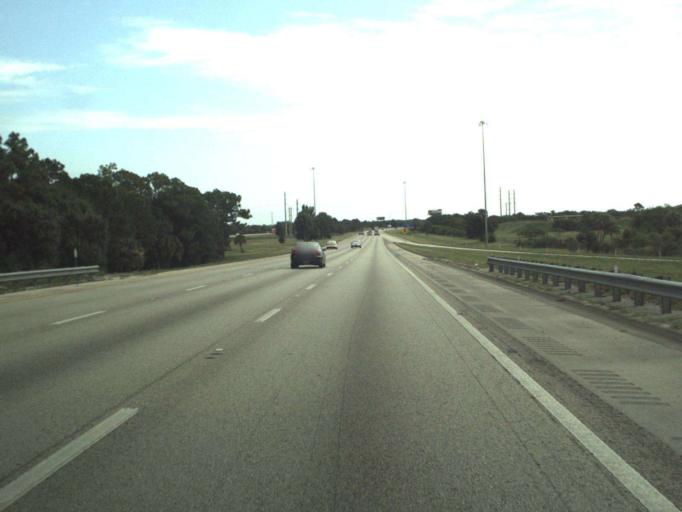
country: US
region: Florida
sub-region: Saint Lucie County
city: Fort Pierce South
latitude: 27.3764
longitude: -80.4080
